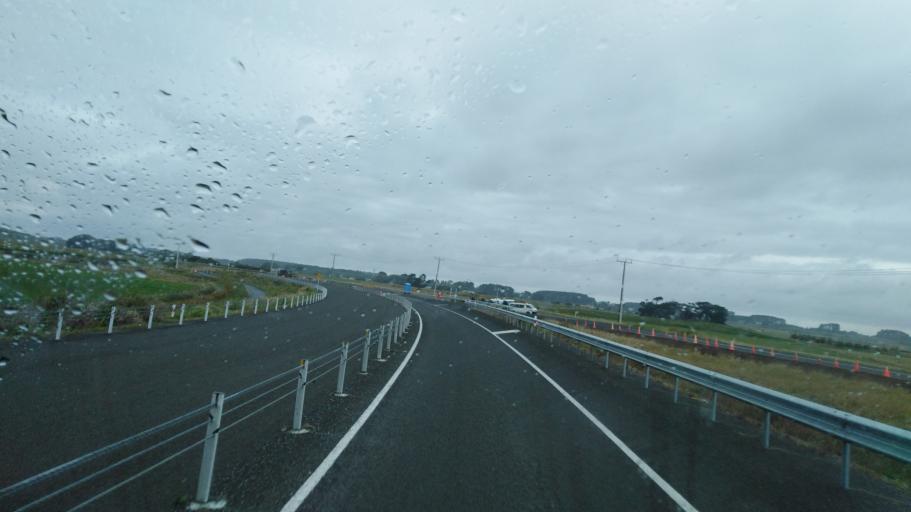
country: NZ
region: Manawatu-Wanganui
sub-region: Horowhenua District
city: Foxton
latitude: -40.5016
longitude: 175.2821
